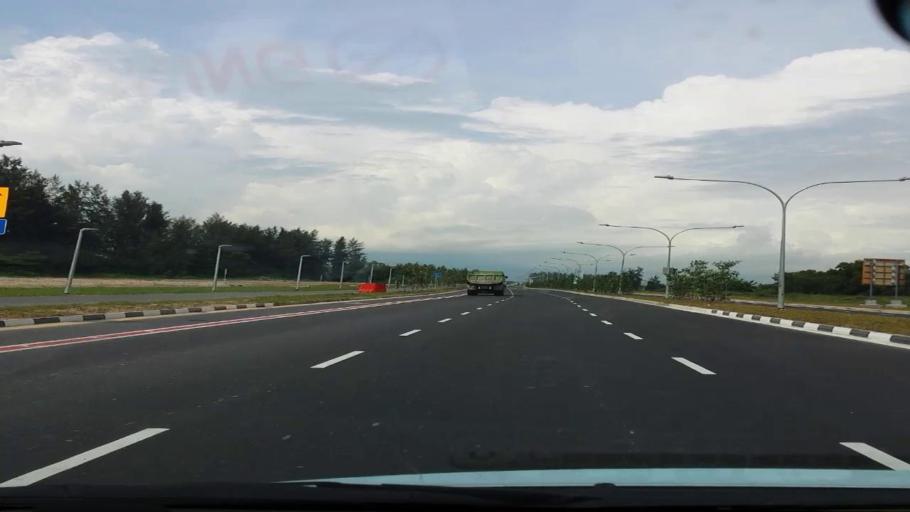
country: SG
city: Singapore
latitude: 1.3385
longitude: 104.0243
